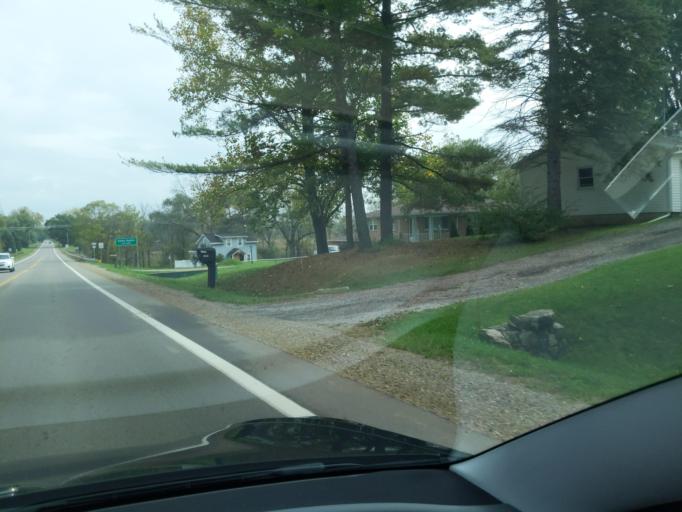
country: US
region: Michigan
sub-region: Eaton County
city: Eaton Rapids
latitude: 42.5182
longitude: -84.6709
